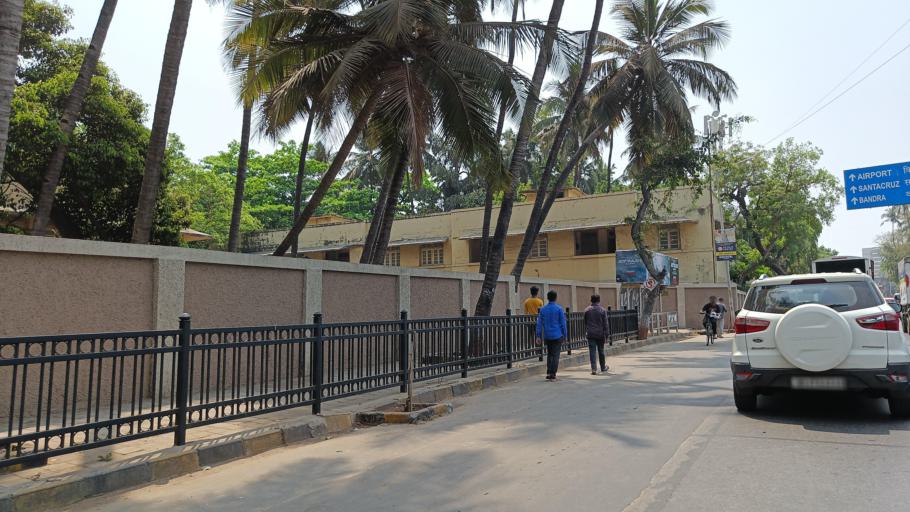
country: IN
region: Maharashtra
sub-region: Mumbai Suburban
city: Mumbai
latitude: 19.0956
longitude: 72.8281
